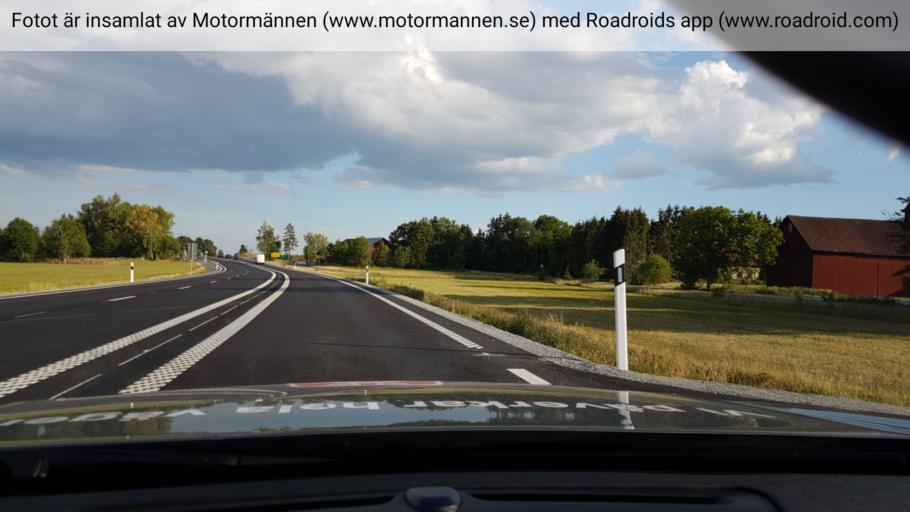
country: SE
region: Uppsala
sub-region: Enkopings Kommun
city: Irsta
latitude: 59.7254
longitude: 16.9586
